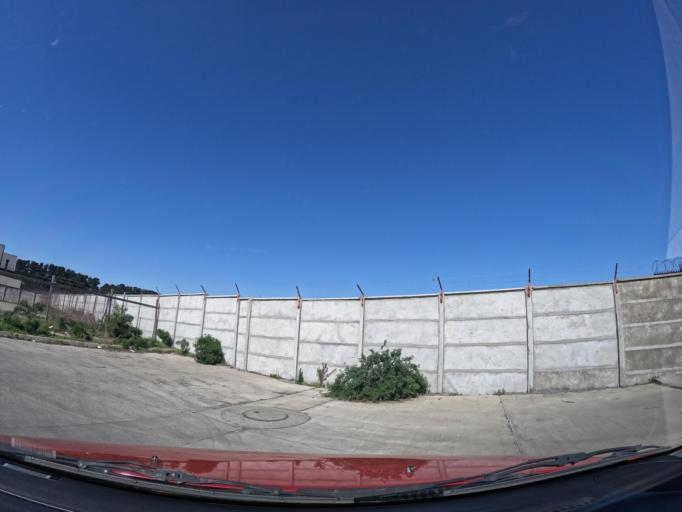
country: CL
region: Biobio
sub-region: Provincia de Concepcion
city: Concepcion
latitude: -36.8914
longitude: -73.1456
